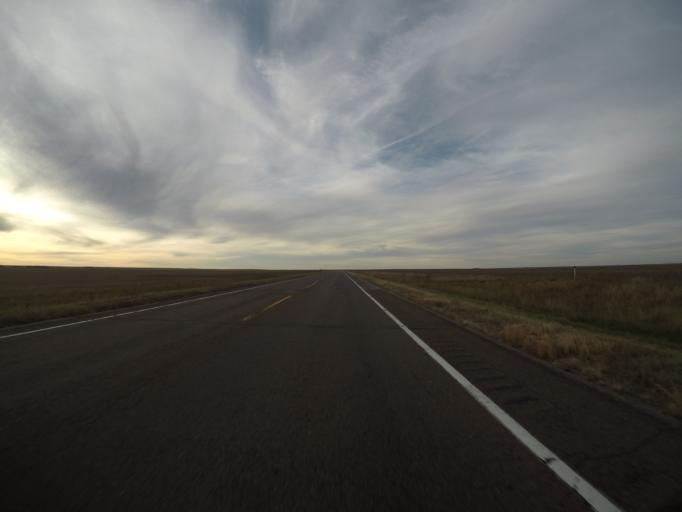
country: US
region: Colorado
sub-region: Yuma County
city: Yuma
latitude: 39.6872
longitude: -102.9752
